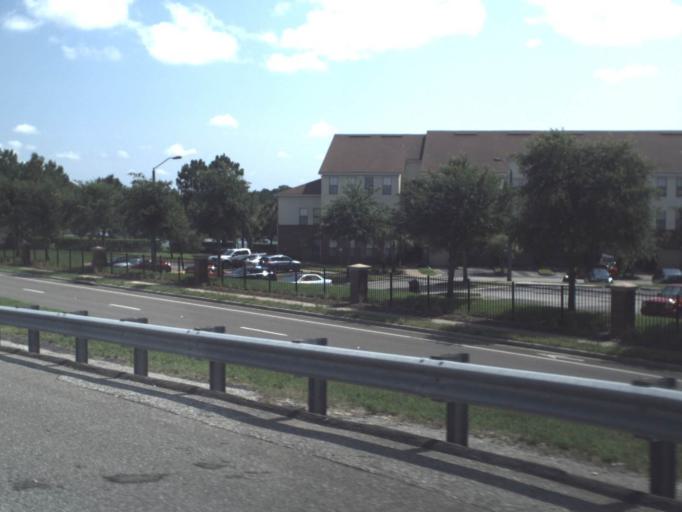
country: US
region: Florida
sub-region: Duval County
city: Jacksonville
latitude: 30.3401
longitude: -81.5521
